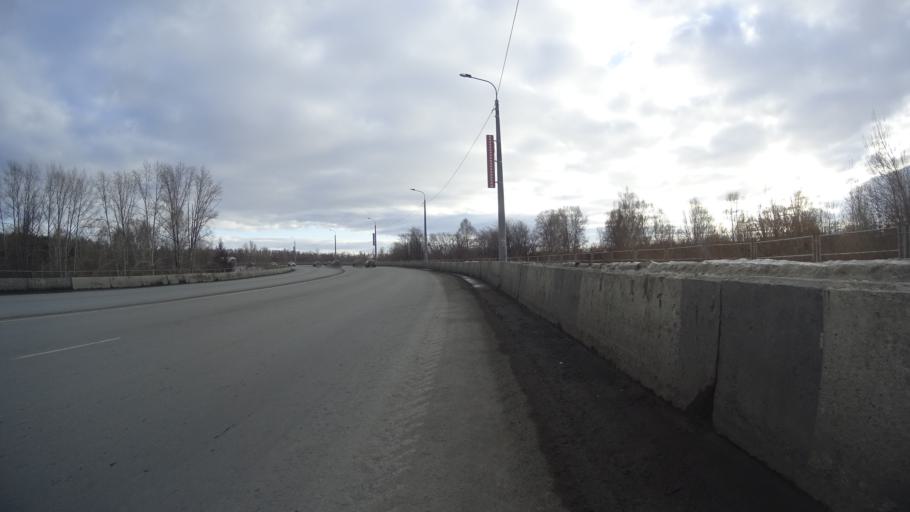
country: RU
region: Chelyabinsk
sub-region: Gorod Chelyabinsk
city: Chelyabinsk
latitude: 55.1506
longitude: 61.3191
